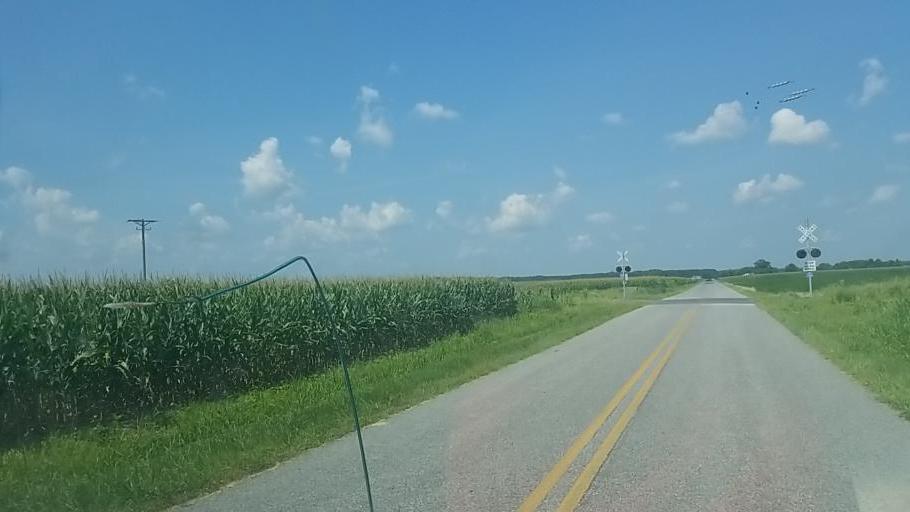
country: US
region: Maryland
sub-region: Worcester County
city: Berlin
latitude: 38.2940
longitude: -75.2507
